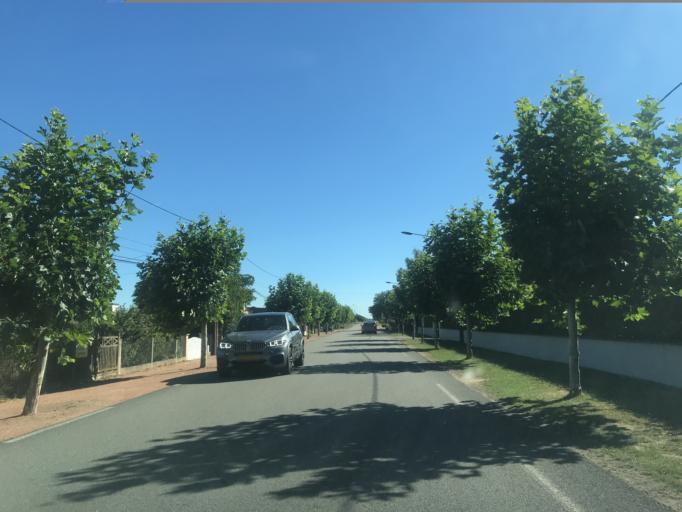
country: FR
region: Limousin
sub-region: Departement de la Creuse
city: Gouzon
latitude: 46.1951
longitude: 2.2468
